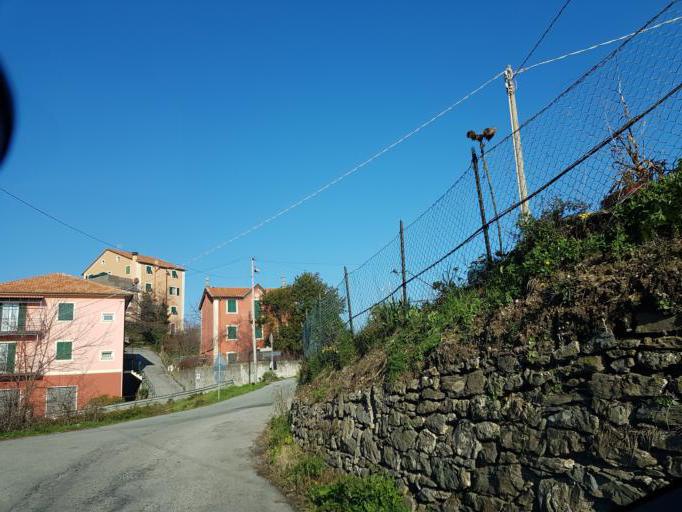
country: IT
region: Liguria
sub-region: Provincia di Genova
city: Campomorone
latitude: 44.5018
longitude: 8.8749
